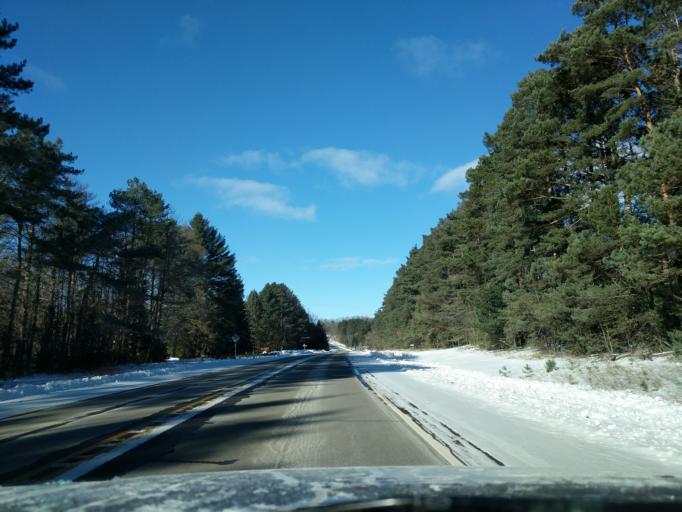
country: US
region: Wisconsin
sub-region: Menominee County
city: Keshena
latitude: 45.1413
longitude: -88.6794
